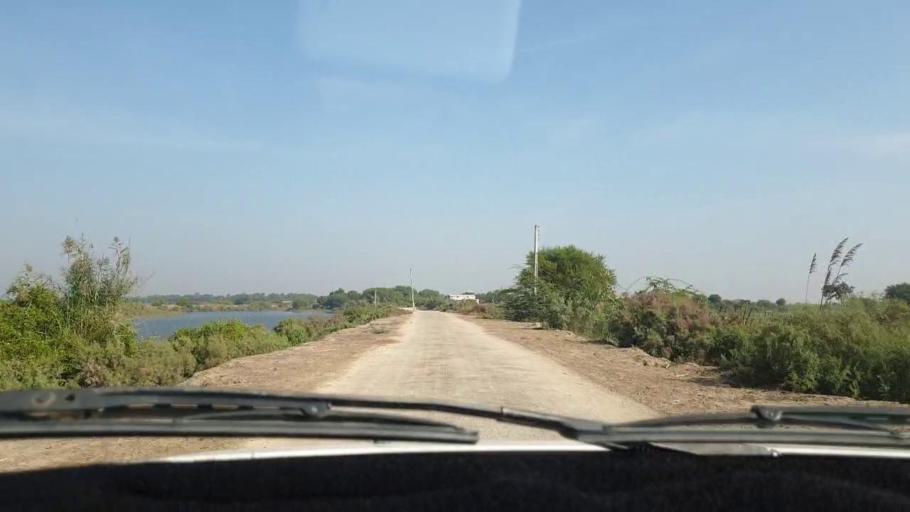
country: PK
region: Sindh
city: Tando Muhammad Khan
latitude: 24.9893
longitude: 68.4635
